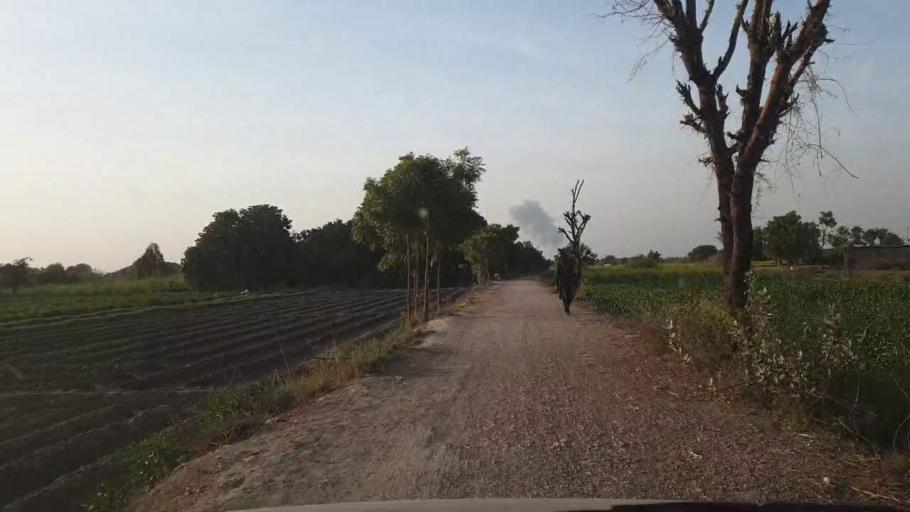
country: PK
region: Sindh
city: Chambar
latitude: 25.2818
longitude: 68.8087
